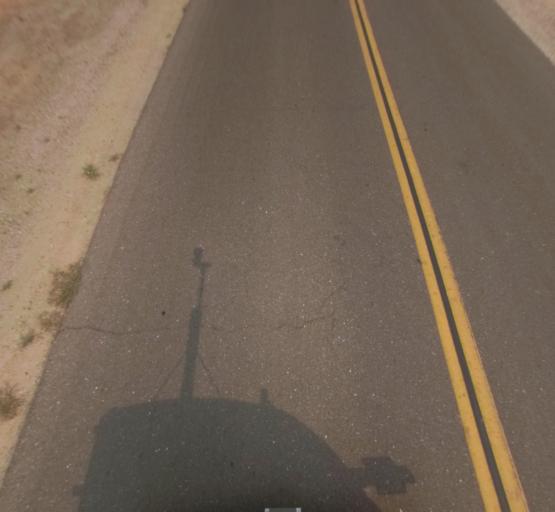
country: US
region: California
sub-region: Madera County
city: Madera Acres
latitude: 37.0151
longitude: -120.0641
